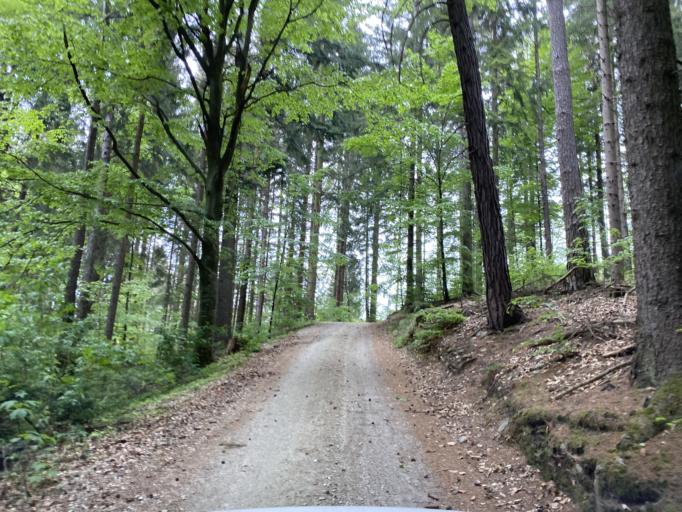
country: AT
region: Styria
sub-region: Politischer Bezirk Weiz
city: Gschaid bei Birkfeld
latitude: 47.3475
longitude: 15.7265
